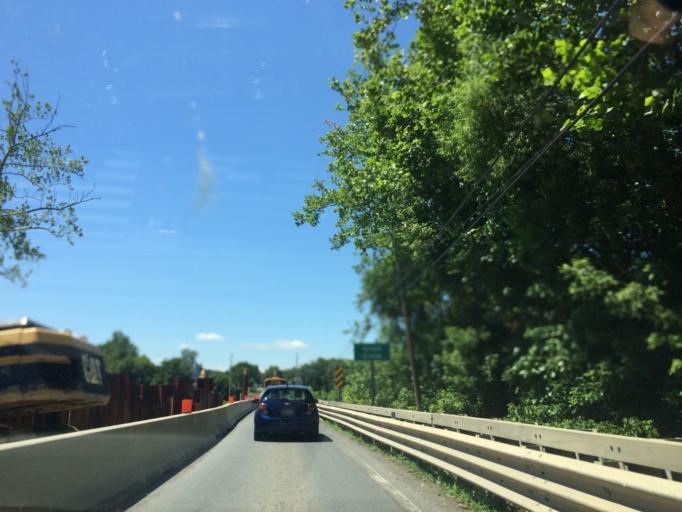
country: US
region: Maryland
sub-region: Frederick County
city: Woodsboro
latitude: 39.5302
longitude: -77.3071
